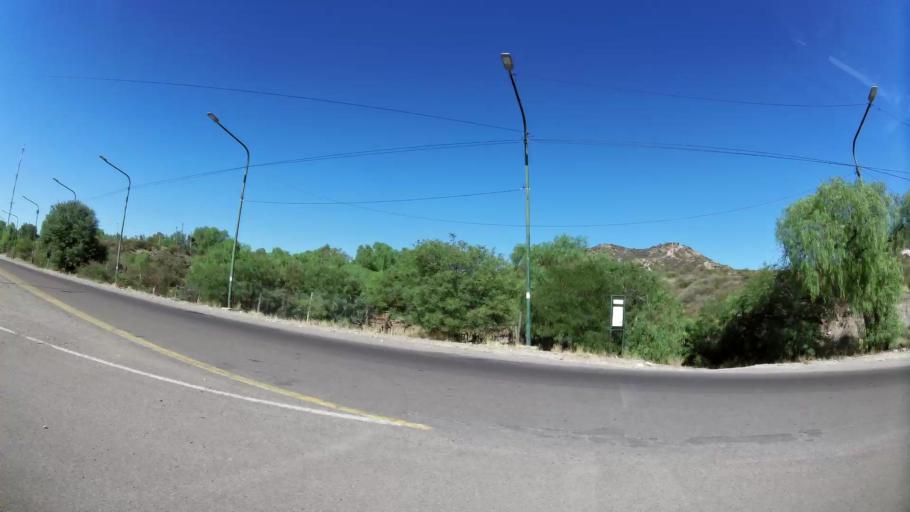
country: AR
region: Mendoza
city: Mendoza
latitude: -32.8918
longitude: -68.8850
